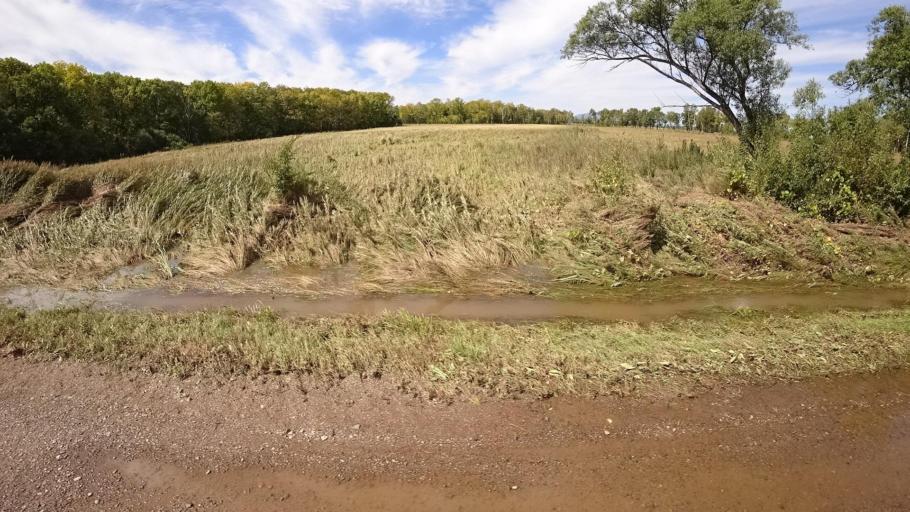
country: RU
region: Primorskiy
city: Yakovlevka
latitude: 44.6615
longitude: 133.7497
